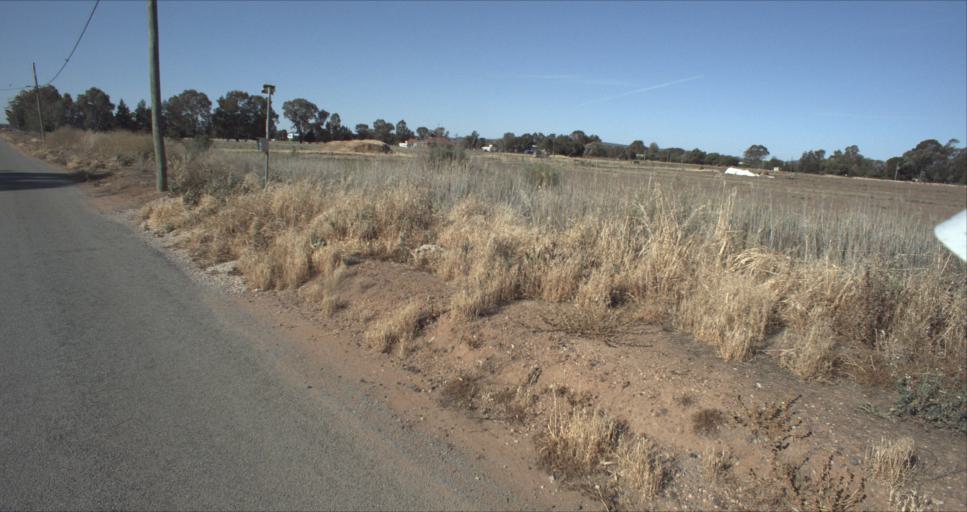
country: AU
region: New South Wales
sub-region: Leeton
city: Leeton
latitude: -34.5400
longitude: 146.4157
